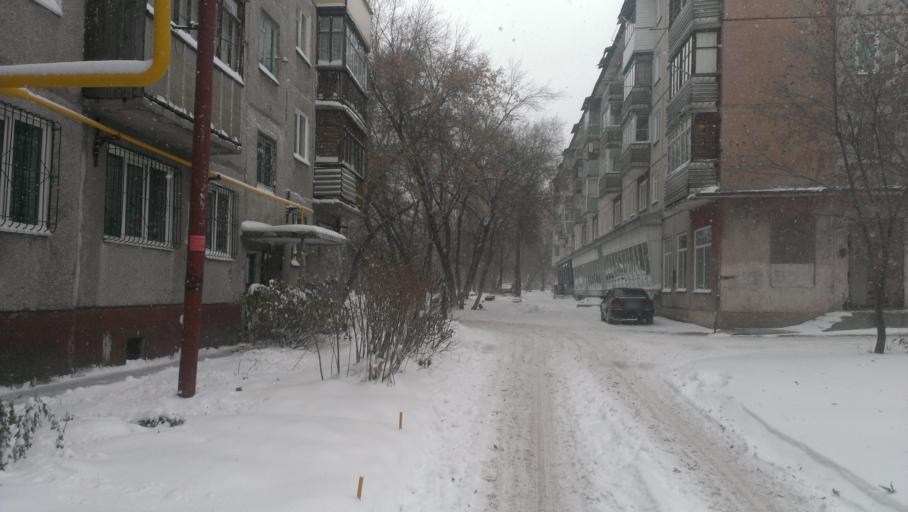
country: RU
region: Altai Krai
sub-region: Gorod Barnaulskiy
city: Barnaul
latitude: 53.3619
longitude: 83.6926
